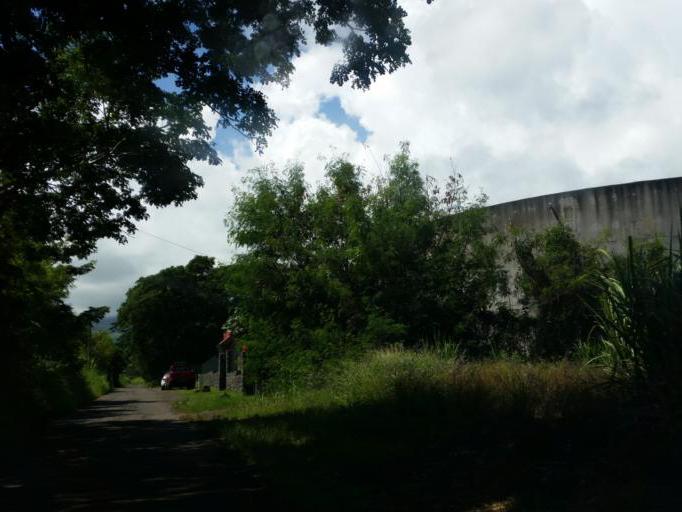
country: RE
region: Reunion
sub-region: Reunion
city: Sainte-Marie
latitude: -20.9077
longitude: 55.5161
